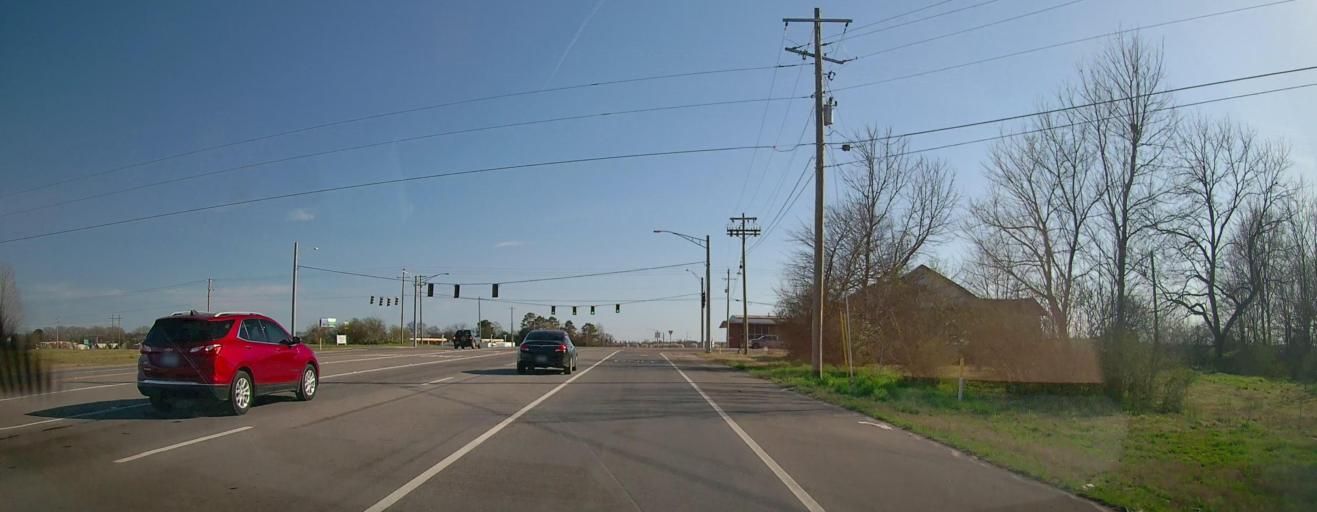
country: US
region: Alabama
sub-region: Colbert County
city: Muscle Shoals
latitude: 34.7016
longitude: -87.6349
